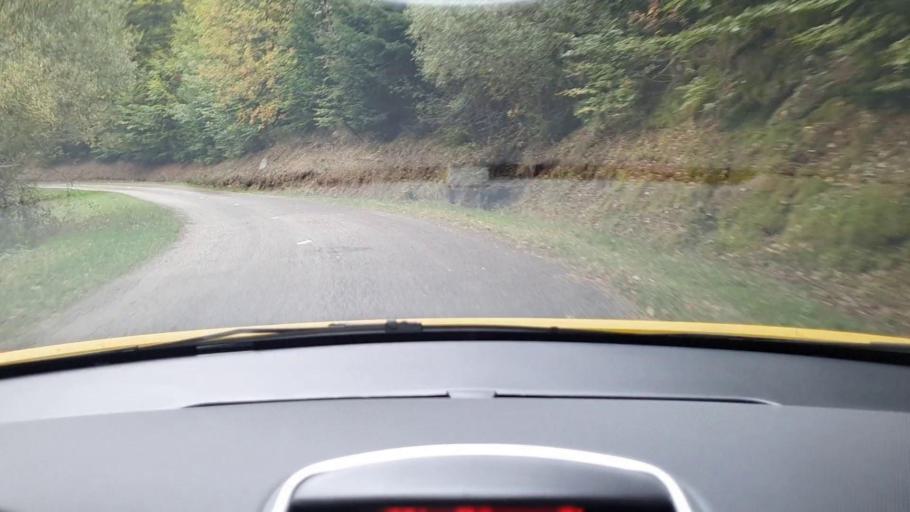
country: FR
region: Languedoc-Roussillon
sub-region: Departement de la Lozere
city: Meyrueis
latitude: 44.0956
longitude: 3.4698
